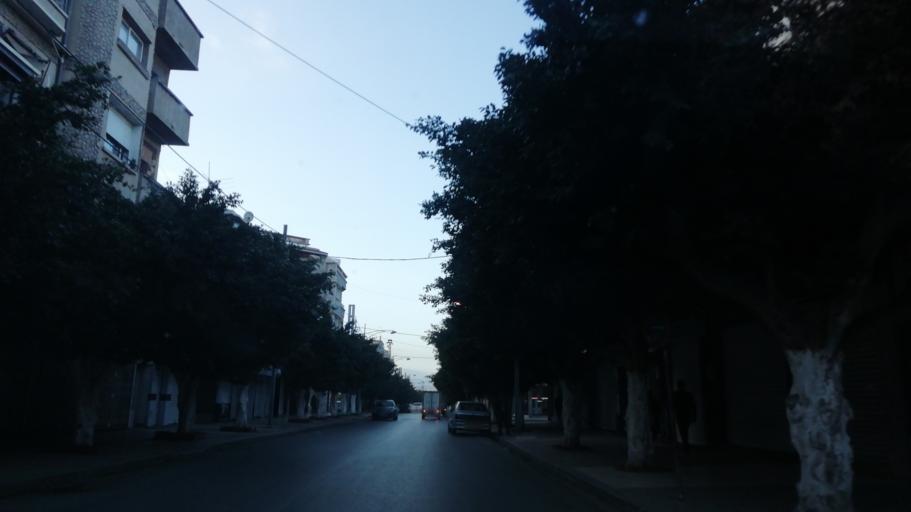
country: DZ
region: Oran
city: Oran
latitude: 35.6809
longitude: -0.6560
